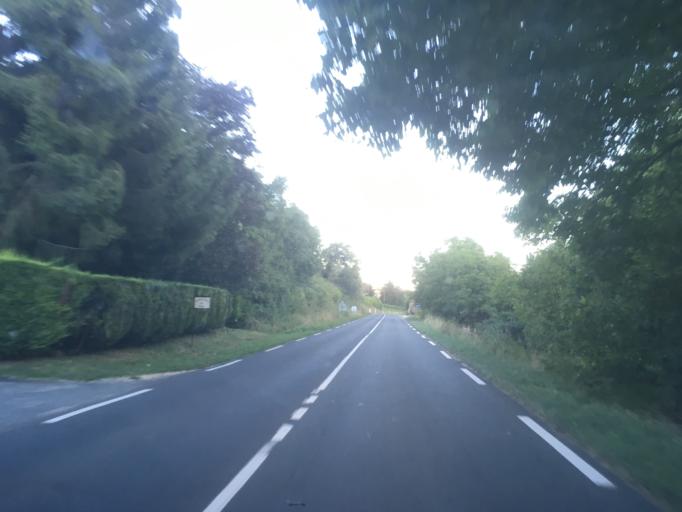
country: FR
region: Aquitaine
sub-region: Departement de la Dordogne
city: Cenac-et-Saint-Julien
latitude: 44.8424
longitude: 1.1710
